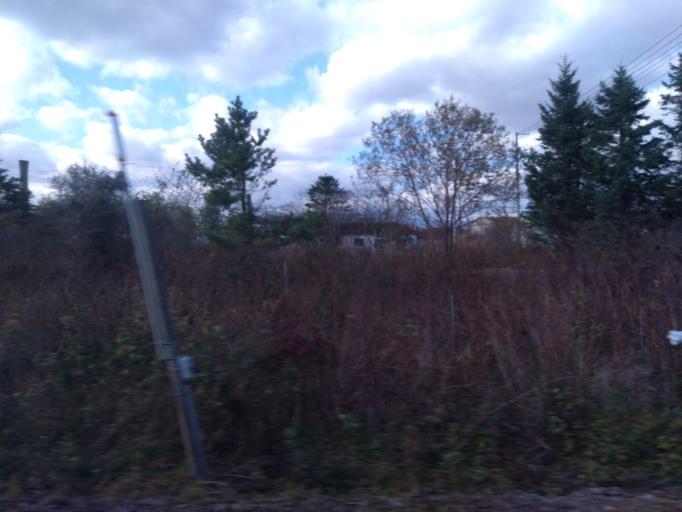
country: JP
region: Hokkaido
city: Shiraoi
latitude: 42.5065
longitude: 141.2822
